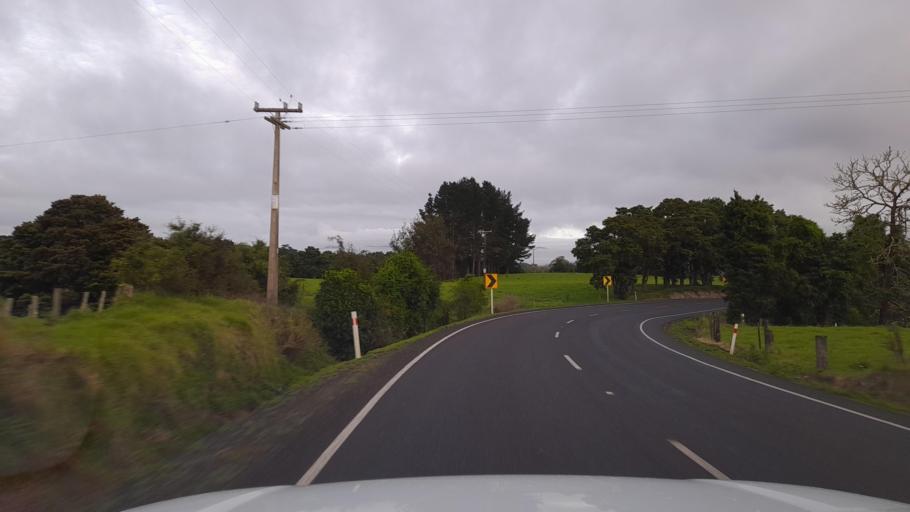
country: NZ
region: Northland
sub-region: Whangarei
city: Maungatapere
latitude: -35.7266
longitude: 174.0435
